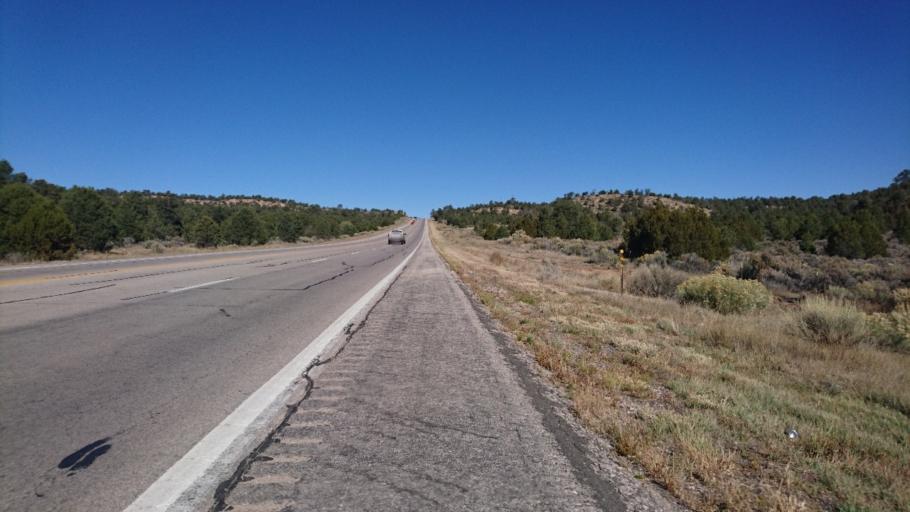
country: US
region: New Mexico
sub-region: McKinley County
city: Black Rock
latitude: 35.2134
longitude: -108.7627
